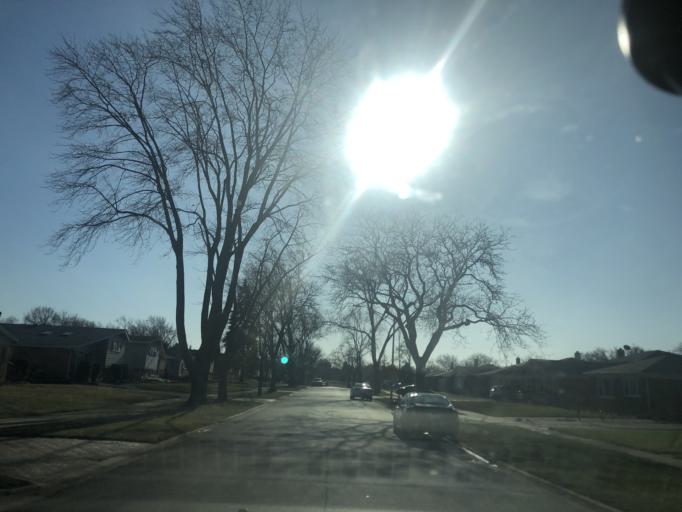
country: US
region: Illinois
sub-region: DuPage County
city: Addison
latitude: 41.9293
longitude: -87.9936
